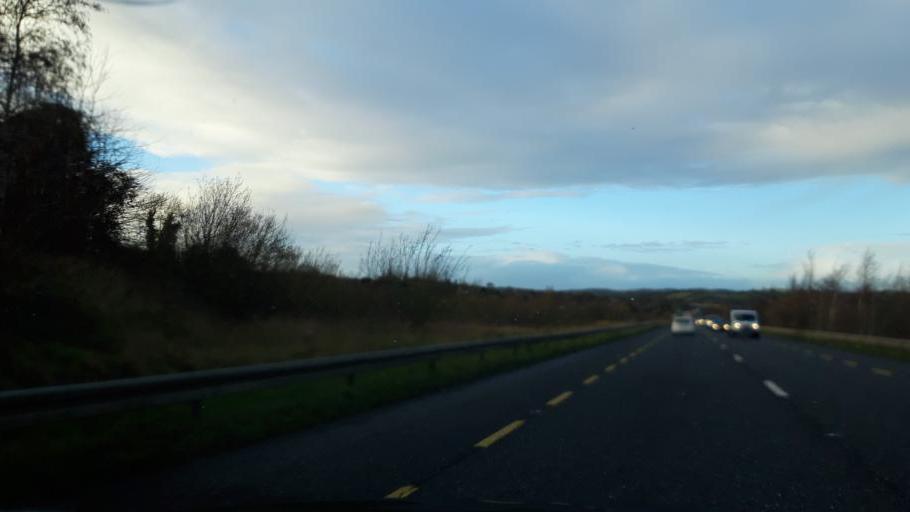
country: IE
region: Ulster
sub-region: County Monaghan
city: Carrickmacross
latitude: 53.9829
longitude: -6.7102
